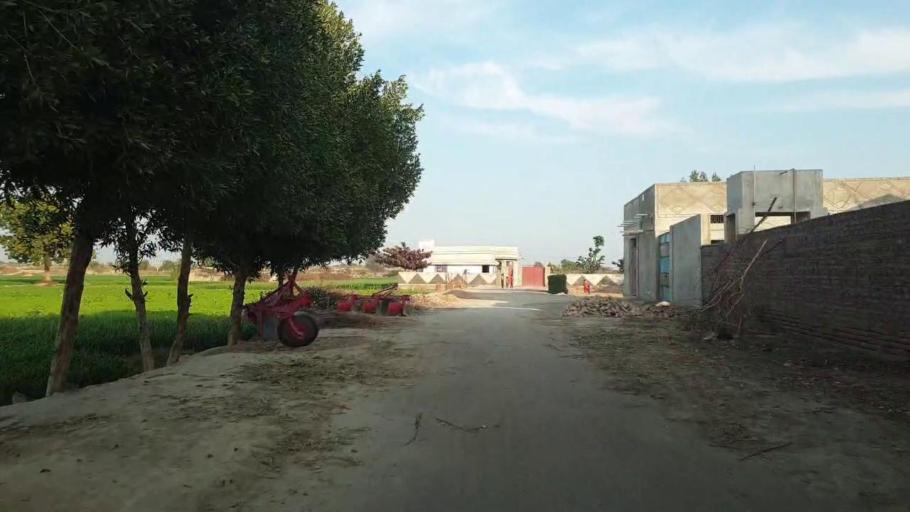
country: PK
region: Sindh
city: Shahpur Chakar
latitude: 26.1612
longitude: 68.6372
